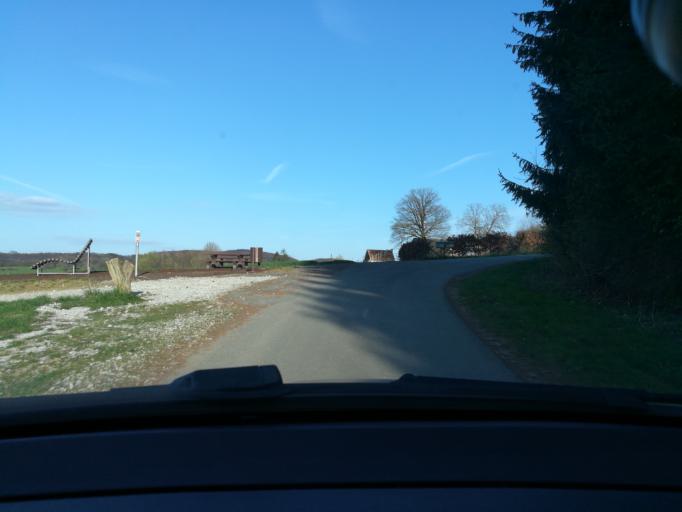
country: DE
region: North Rhine-Westphalia
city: Borgholzhausen
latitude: 52.0914
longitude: 8.2951
